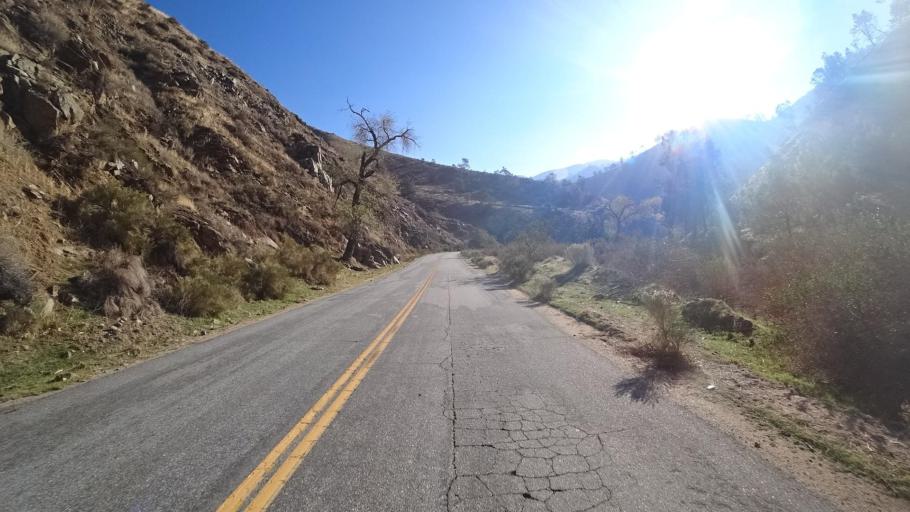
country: US
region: California
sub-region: Kern County
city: Golden Hills
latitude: 35.3171
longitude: -118.5381
